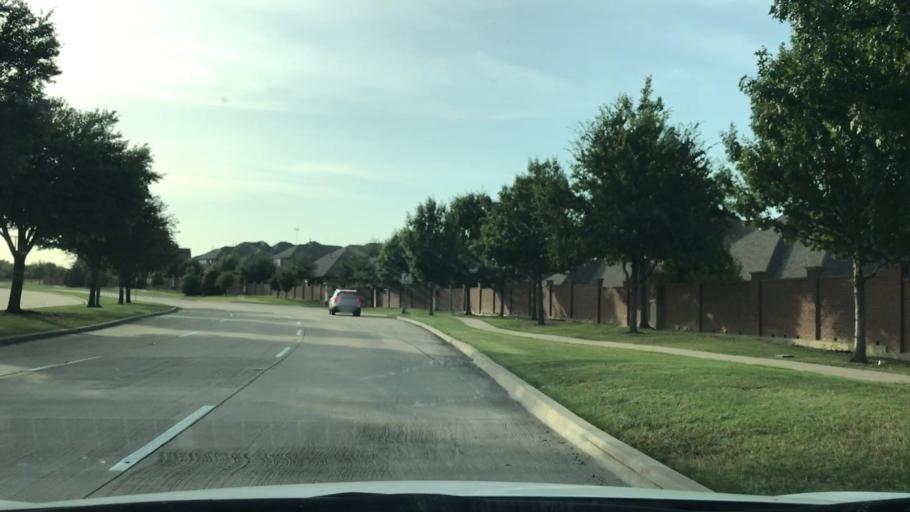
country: US
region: Texas
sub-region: Dallas County
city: Farmers Branch
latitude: 32.9045
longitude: -96.9483
